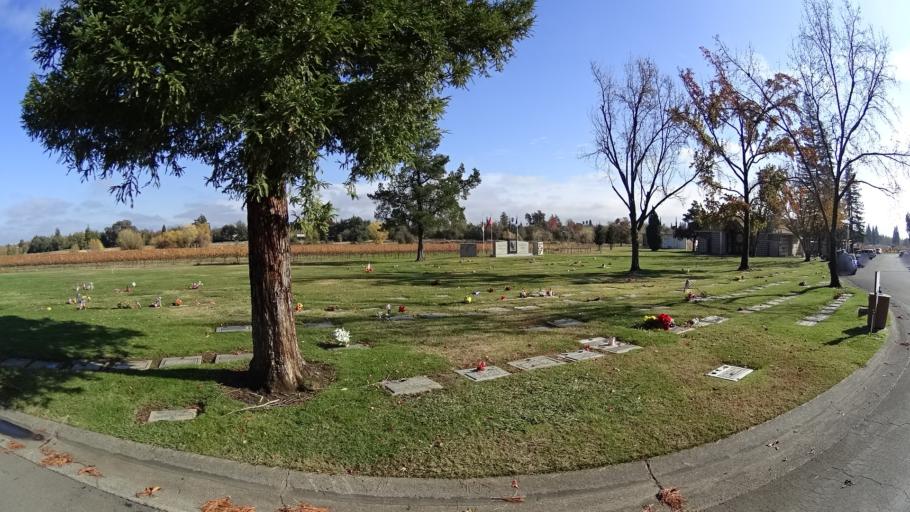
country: US
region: California
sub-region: Sacramento County
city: Antelope
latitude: 38.6955
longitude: -121.3213
